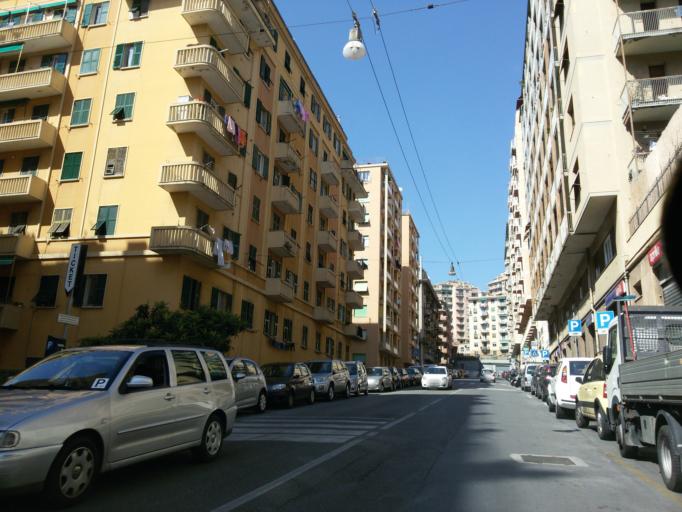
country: IT
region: Liguria
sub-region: Provincia di Genova
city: Genoa
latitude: 44.4116
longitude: 8.9565
